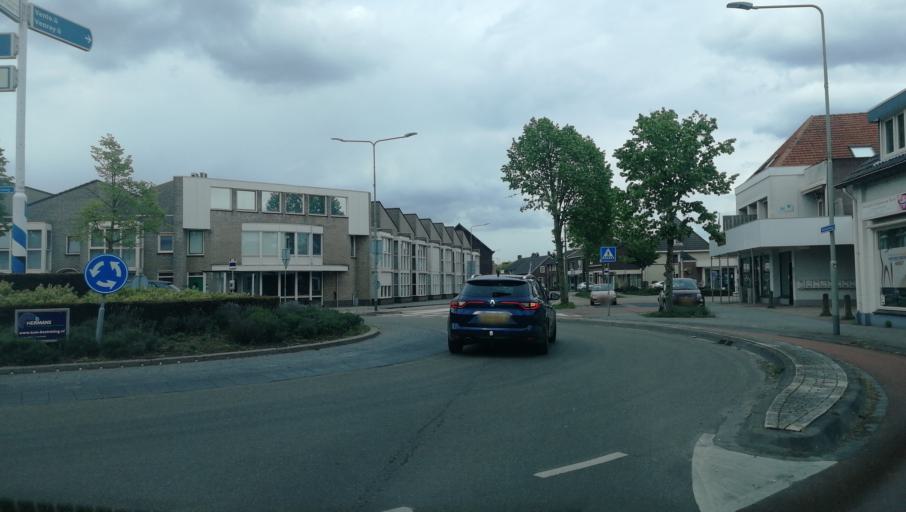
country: NL
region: Limburg
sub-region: Gemeente Peel en Maas
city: Maasbree
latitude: 51.4571
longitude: 6.0505
